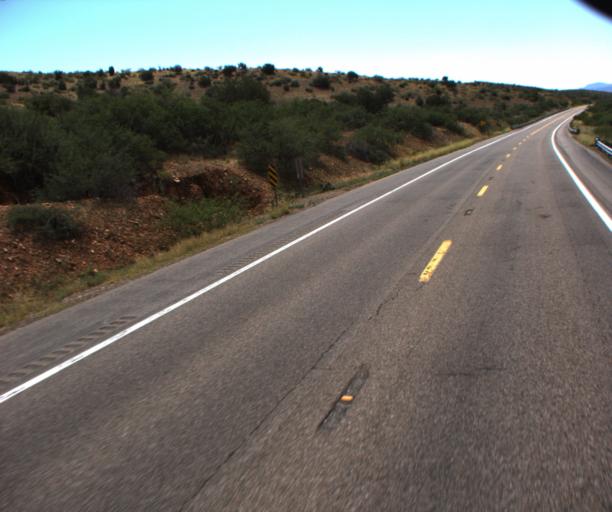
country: US
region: Arizona
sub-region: Gila County
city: Globe
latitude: 33.4700
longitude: -110.7222
